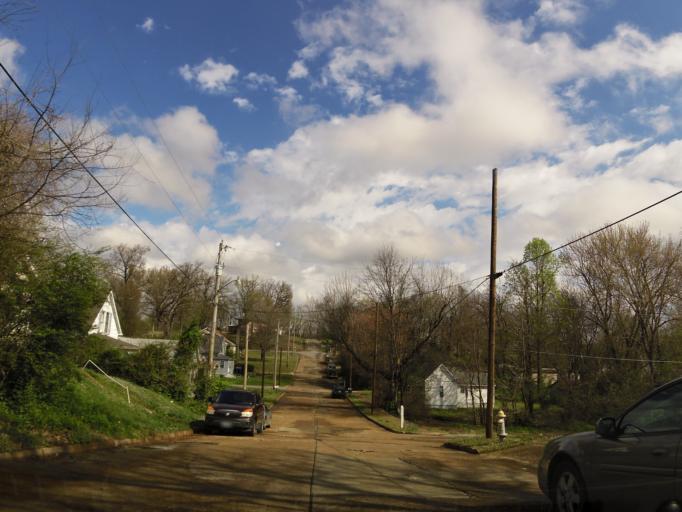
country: US
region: Missouri
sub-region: Butler County
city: Poplar Bluff
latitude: 36.7630
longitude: -90.3936
